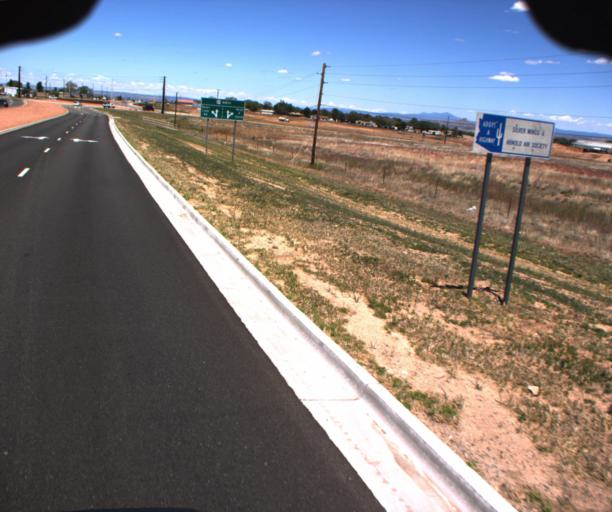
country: US
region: Arizona
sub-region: Yavapai County
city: Chino Valley
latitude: 34.7143
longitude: -112.4529
